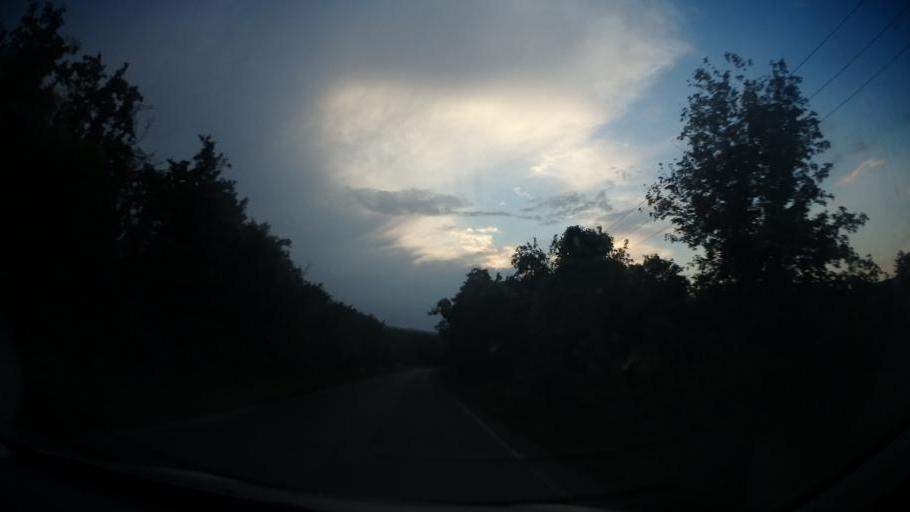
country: CZ
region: South Moravian
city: Dolni Kounice
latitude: 49.0702
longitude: 16.4802
